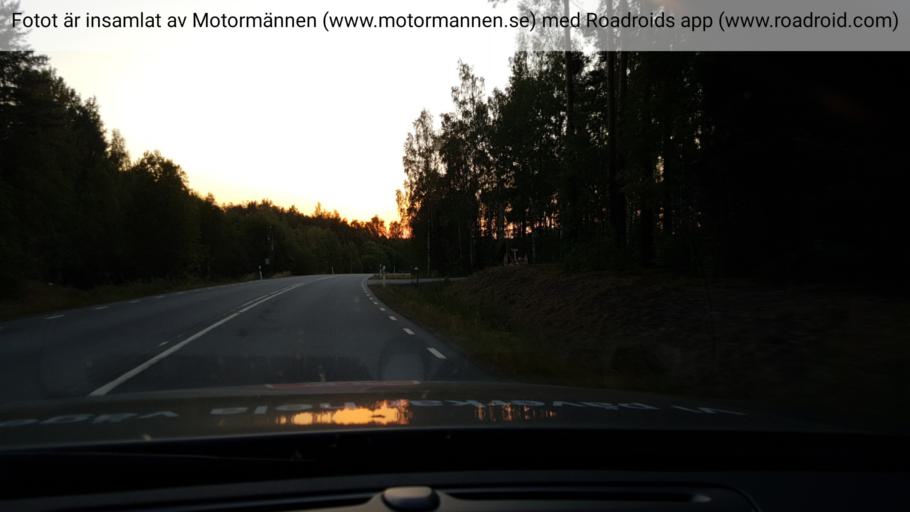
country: SE
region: Uppsala
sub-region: Heby Kommun
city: OEstervala
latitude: 60.1444
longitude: 17.2052
